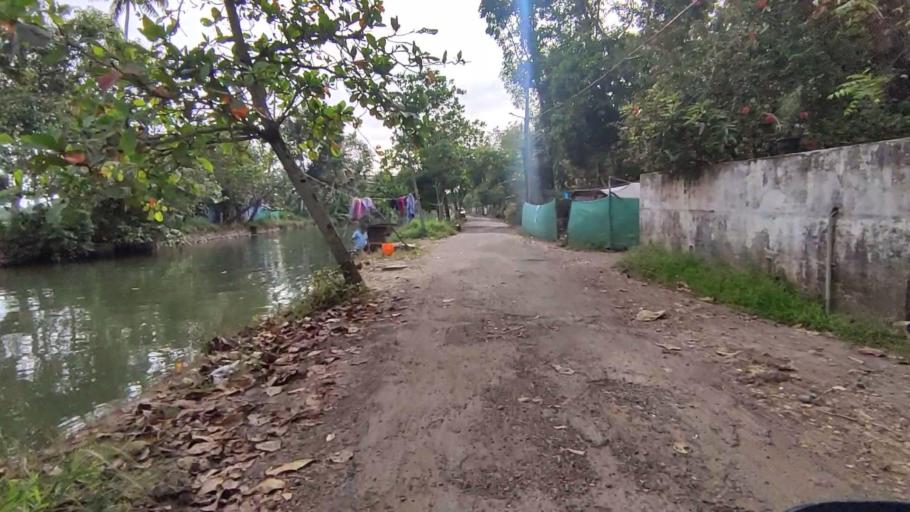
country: IN
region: Kerala
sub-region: Kottayam
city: Kottayam
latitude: 9.5705
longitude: 76.4940
